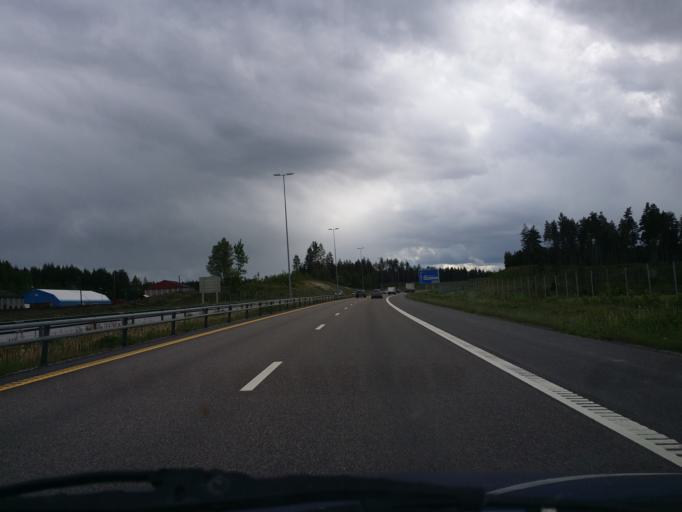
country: NO
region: Akershus
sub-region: Ullensaker
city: Jessheim
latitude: 60.1961
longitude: 11.1898
